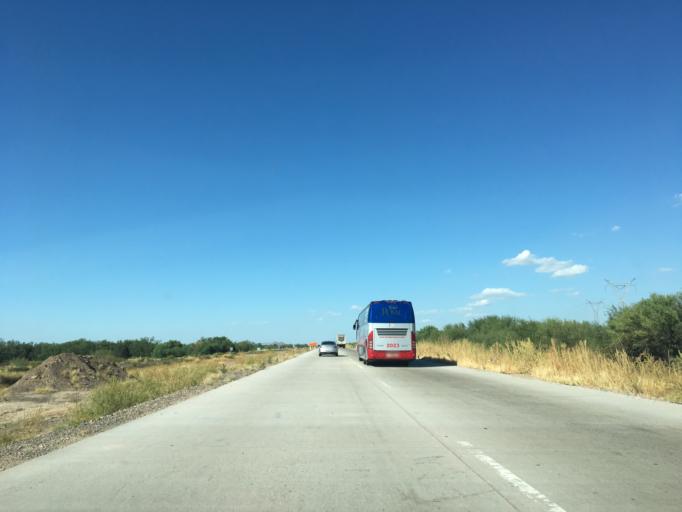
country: MX
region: Sonora
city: Hermosillo
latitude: 28.6823
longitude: -110.9920
